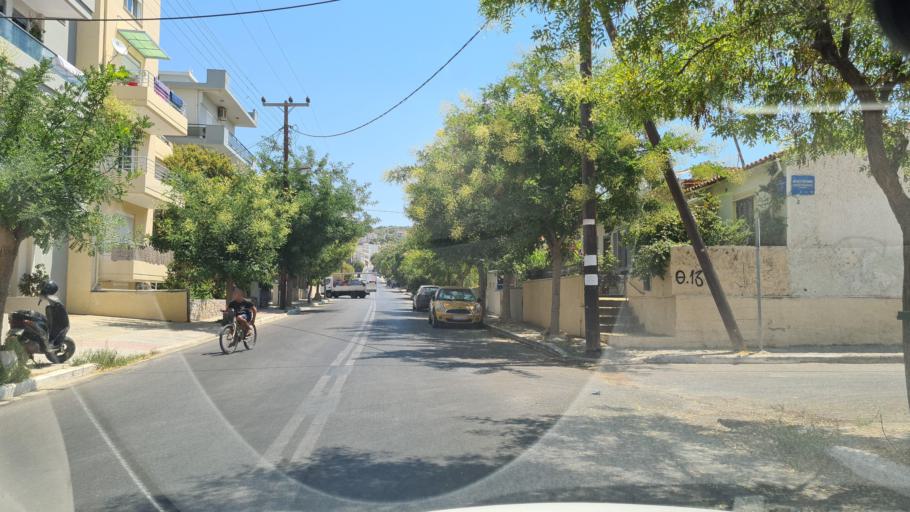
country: GR
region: Crete
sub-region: Nomos Chanias
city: Chania
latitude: 35.5197
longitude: 24.0431
